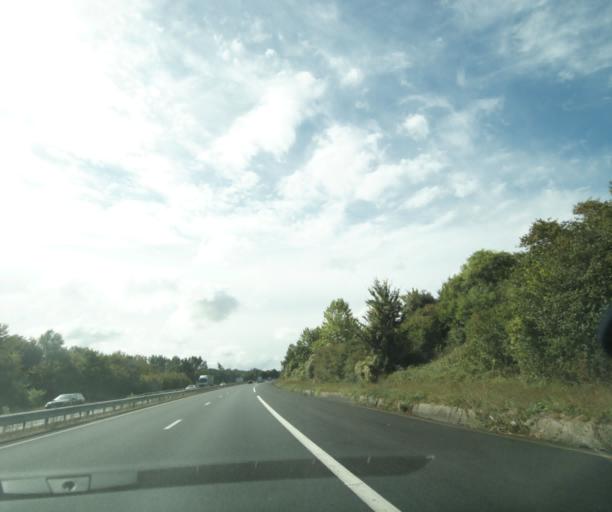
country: FR
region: Poitou-Charentes
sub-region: Departement de la Charente-Maritime
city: Pons
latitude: 45.5938
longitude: -0.5903
